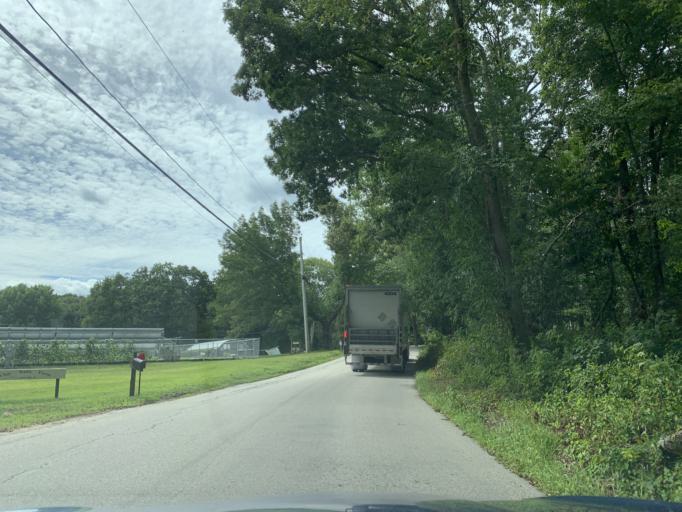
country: US
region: Rhode Island
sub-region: Kent County
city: West Greenwich
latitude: 41.5644
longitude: -71.6206
